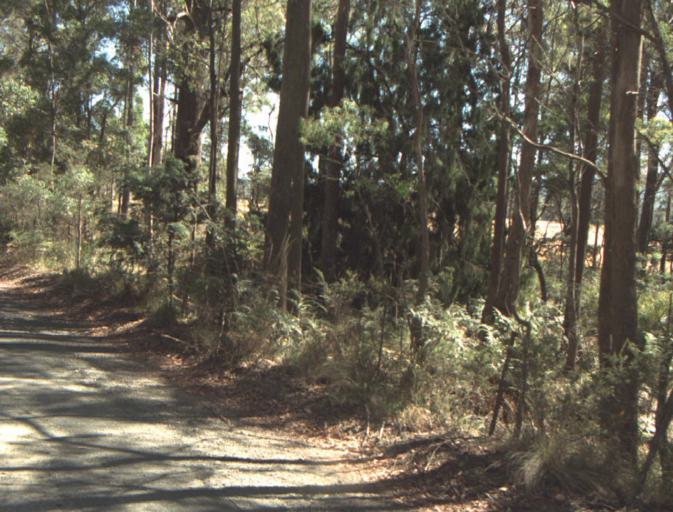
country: AU
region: Tasmania
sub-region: Launceston
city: Newstead
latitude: -41.3620
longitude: 147.2295
